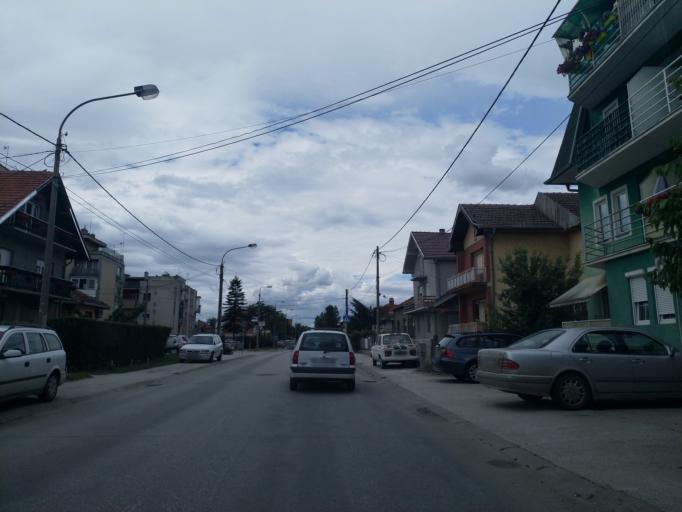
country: RS
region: Central Serbia
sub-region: Pomoravski Okrug
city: Jagodina
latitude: 43.9716
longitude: 21.2742
